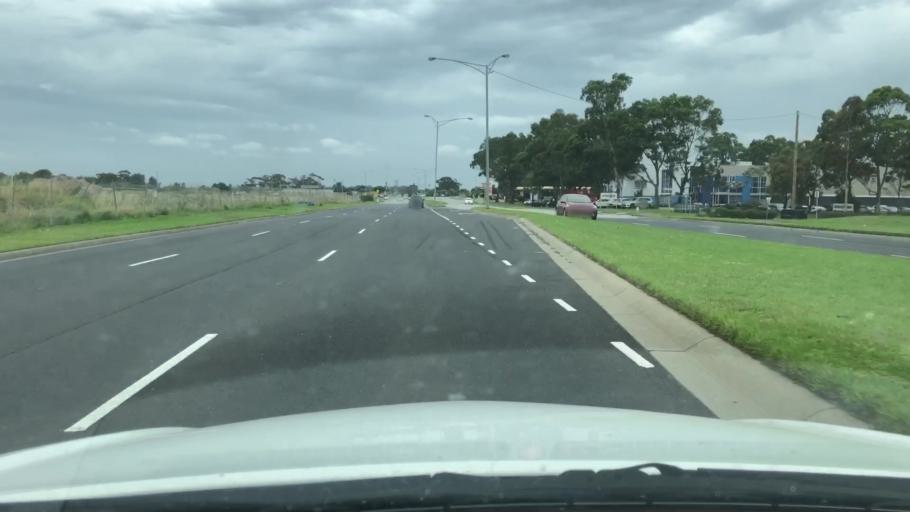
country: AU
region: Victoria
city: Heatherton
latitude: -37.9761
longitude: 145.1111
